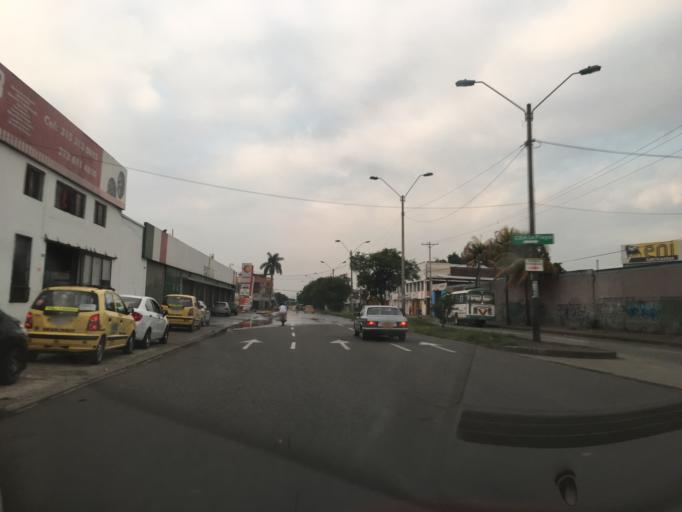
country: CO
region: Valle del Cauca
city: Cali
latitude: 3.4431
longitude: -76.5193
